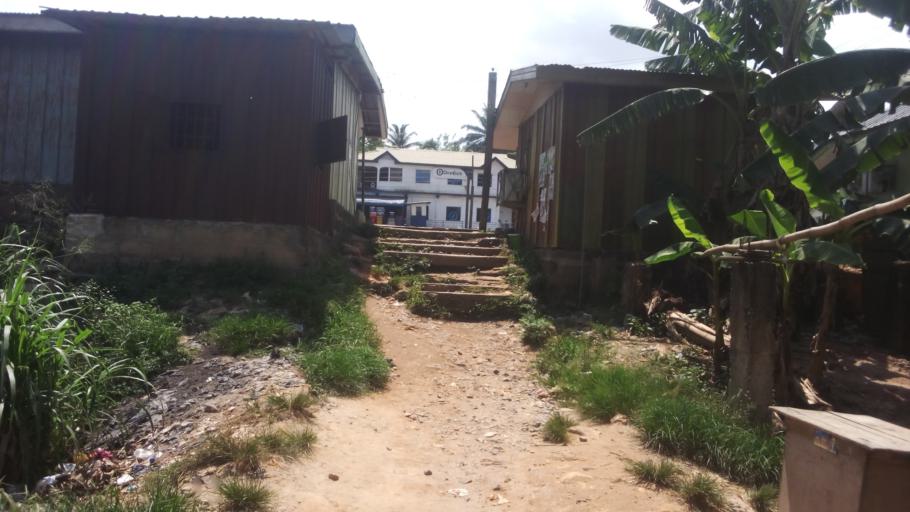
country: GH
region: Western
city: Tarkwa
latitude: 5.3019
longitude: -1.9975
